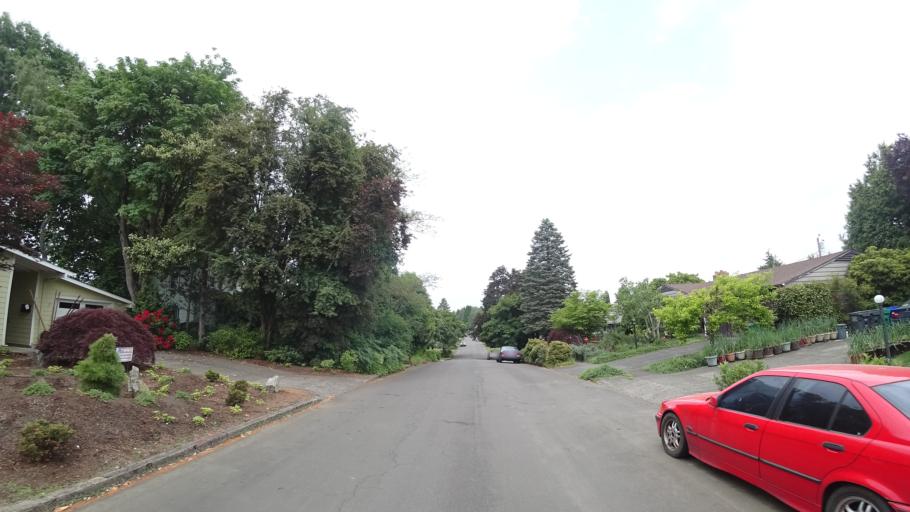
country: US
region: Oregon
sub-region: Clackamas County
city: Milwaukie
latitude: 45.4853
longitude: -122.6289
